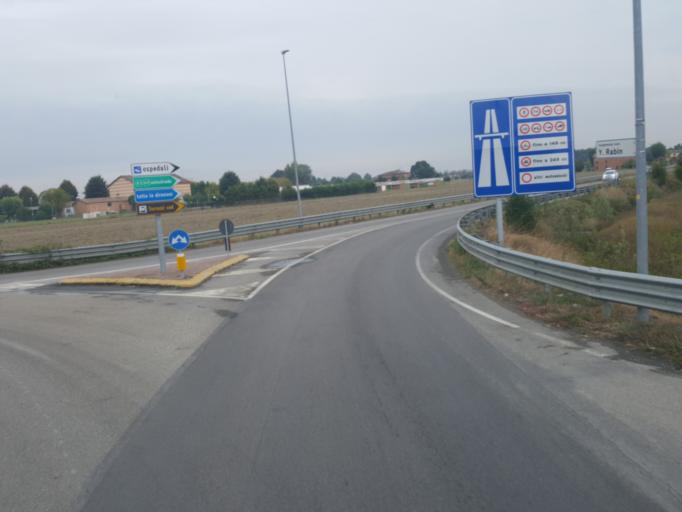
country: IT
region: Emilia-Romagna
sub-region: Provincia di Modena
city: Albareto
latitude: 44.6559
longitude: 10.9703
